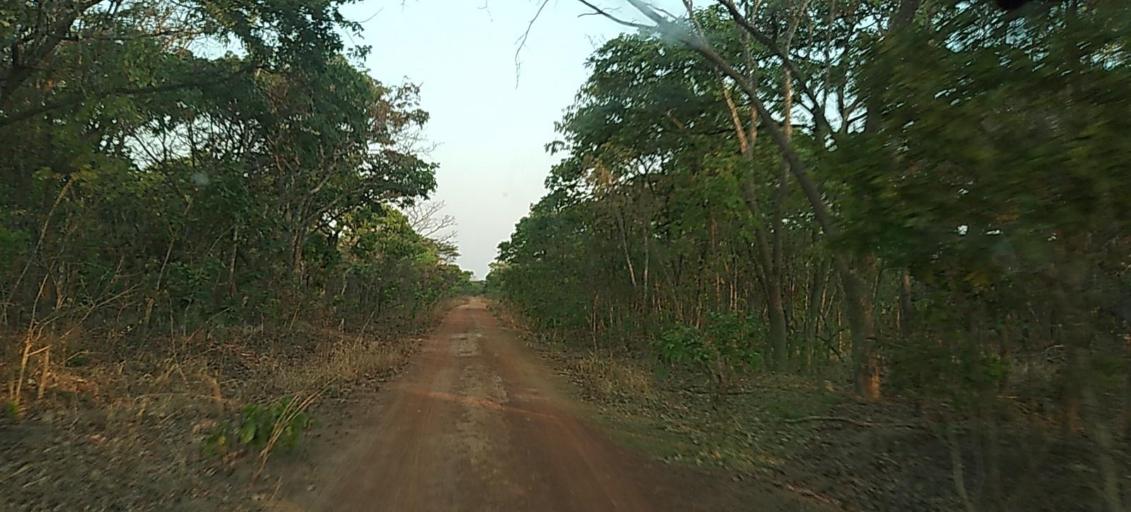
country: ZM
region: North-Western
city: Kalengwa
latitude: -13.1179
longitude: 25.1731
